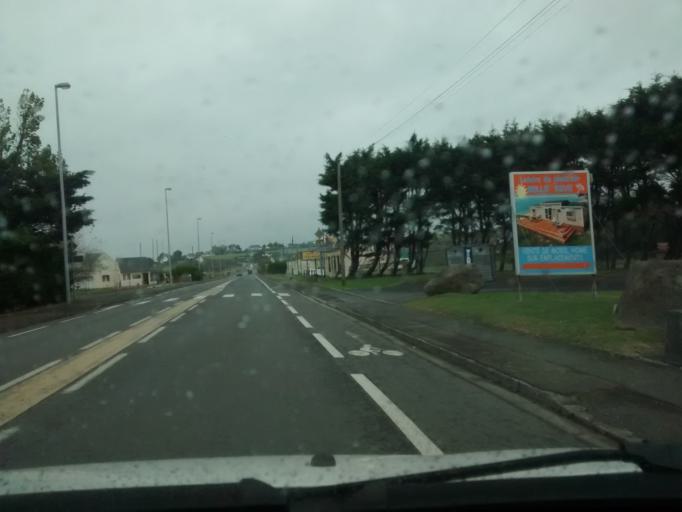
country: FR
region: Lower Normandy
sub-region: Departement de la Manche
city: Saint-Pair-sur-Mer
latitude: 48.8001
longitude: -1.5663
